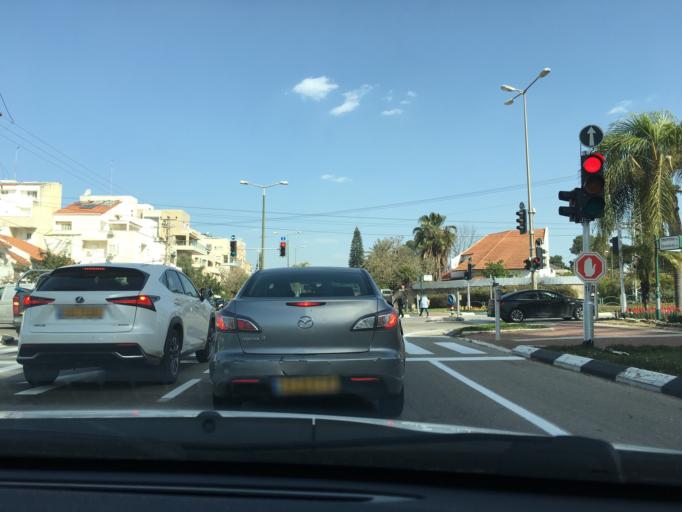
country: IL
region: Central District
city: Kfar Saba
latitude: 32.1783
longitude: 34.8948
